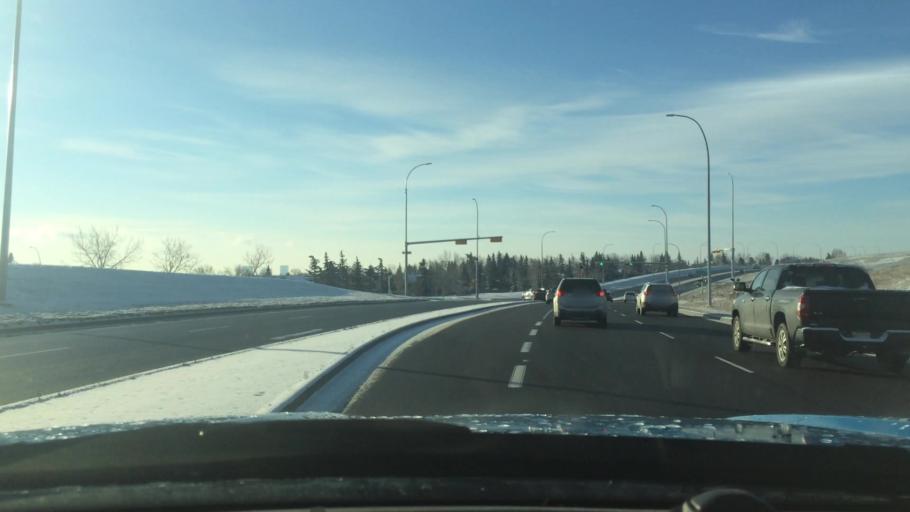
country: CA
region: Alberta
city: Calgary
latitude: 51.1102
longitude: -114.0833
